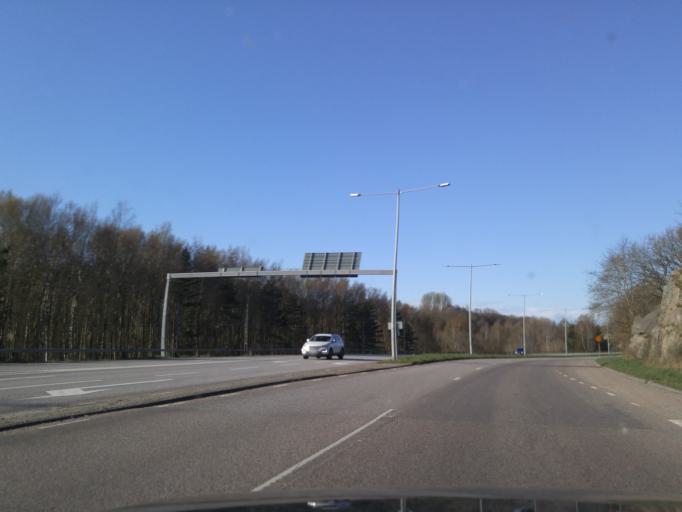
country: SE
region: Vaestra Goetaland
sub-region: Goteborg
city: Hammarkullen
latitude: 57.7664
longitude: 12.0199
